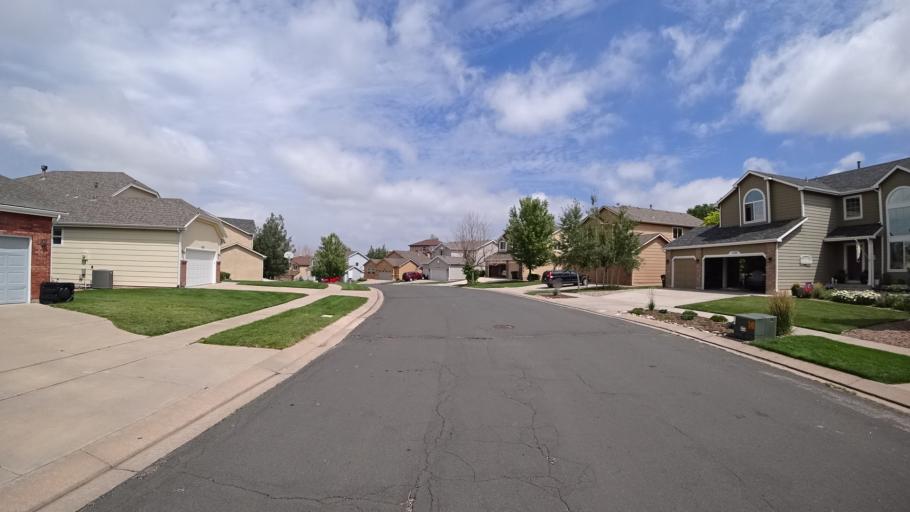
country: US
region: Colorado
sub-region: El Paso County
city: Gleneagle
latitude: 39.0093
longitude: -104.7996
